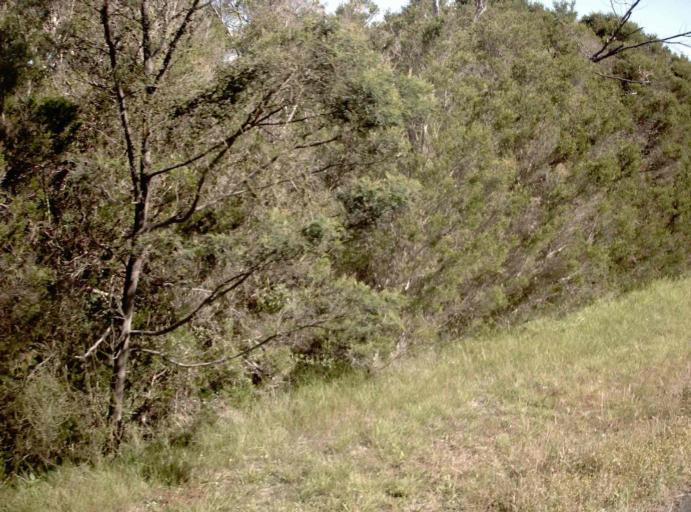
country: AU
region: Victoria
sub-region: Latrobe
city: Traralgon
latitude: -38.6403
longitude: 146.6717
